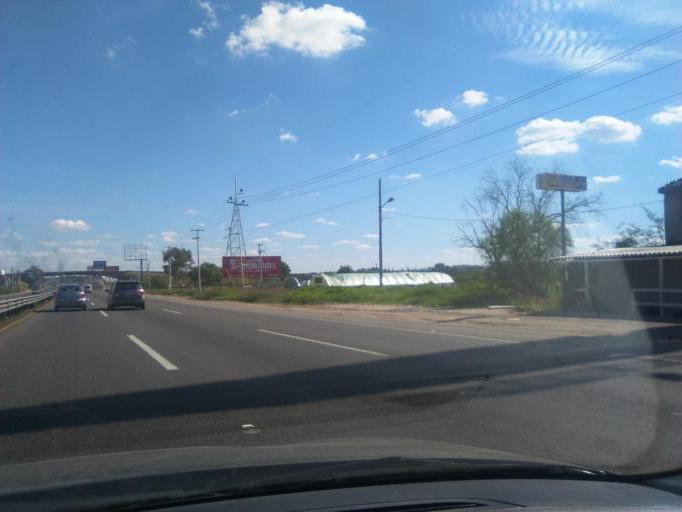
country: MX
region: Guanajuato
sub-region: Silao de la Victoria
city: El Refugio de los Sauces
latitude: 21.0097
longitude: -101.5206
